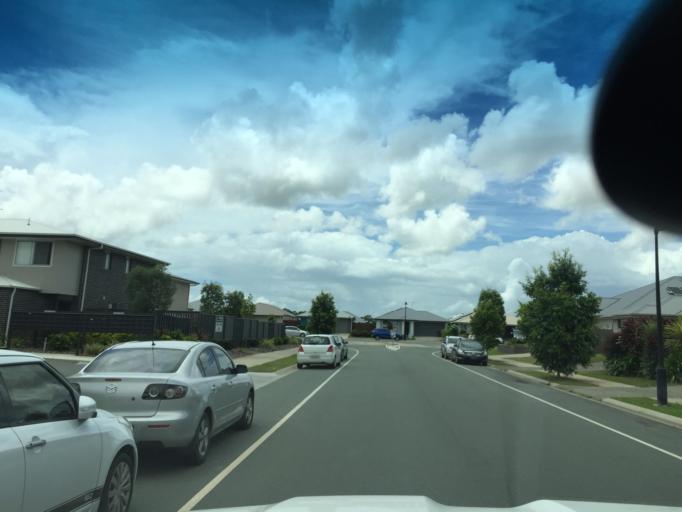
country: AU
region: Queensland
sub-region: Moreton Bay
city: Caboolture South
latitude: -27.0960
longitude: 152.9583
